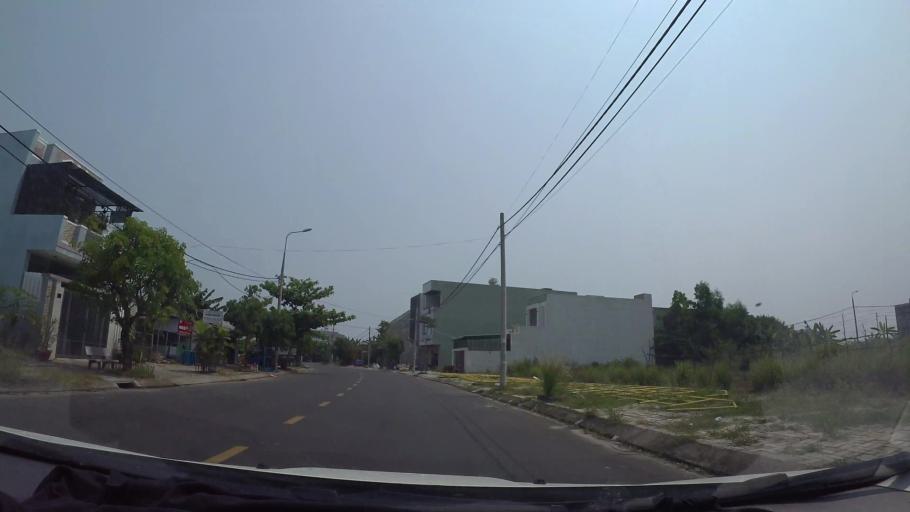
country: VN
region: Da Nang
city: Cam Le
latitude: 16.0001
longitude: 108.2188
